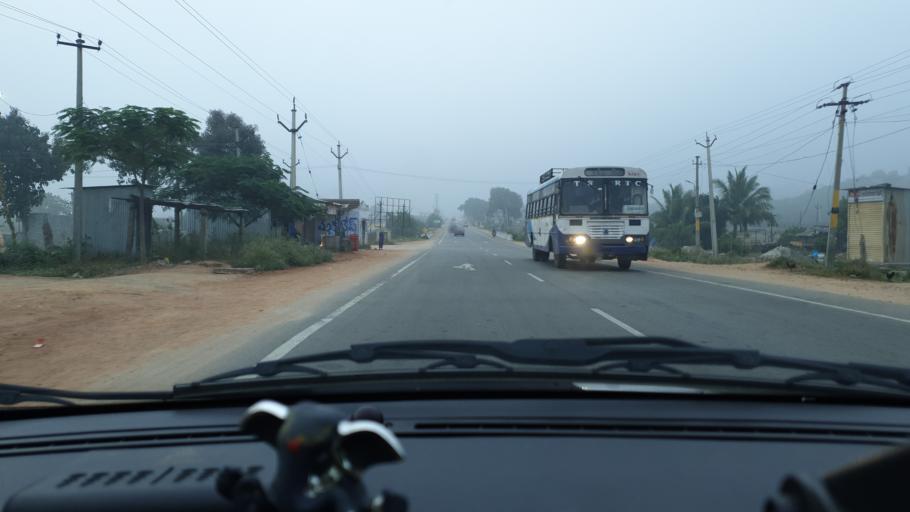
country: IN
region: Telangana
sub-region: Mahbubnagar
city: Farrukhnagar
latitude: 16.9249
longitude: 78.5273
